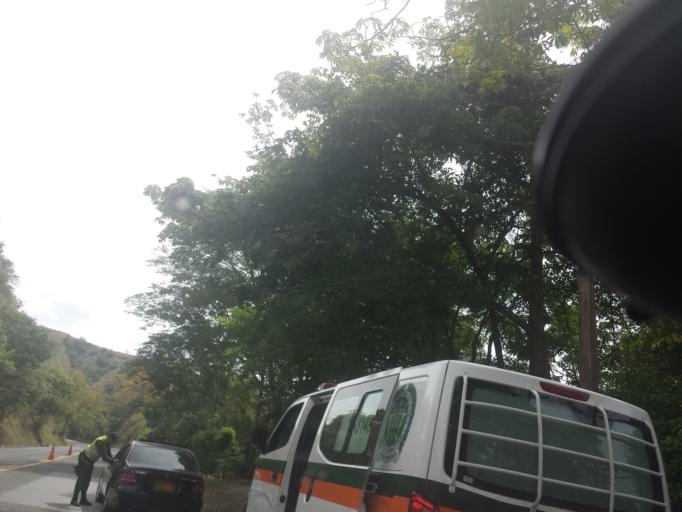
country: CO
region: Antioquia
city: Antioquia
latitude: 6.5723
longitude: -75.8391
